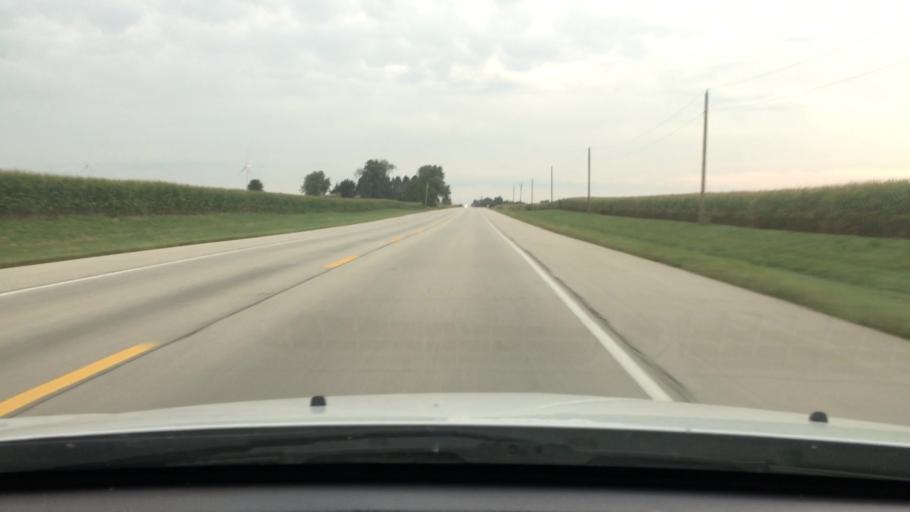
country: US
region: Illinois
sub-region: DeKalb County
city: Waterman
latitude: 41.8067
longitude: -88.7539
